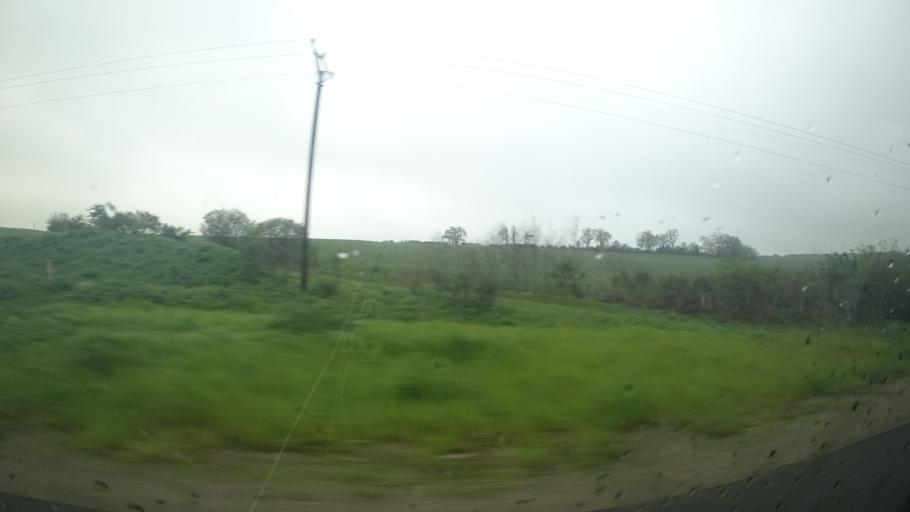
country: FR
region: Midi-Pyrenees
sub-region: Departement de l'Aveyron
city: Severac-le-Chateau
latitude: 44.2502
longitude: 2.9278
